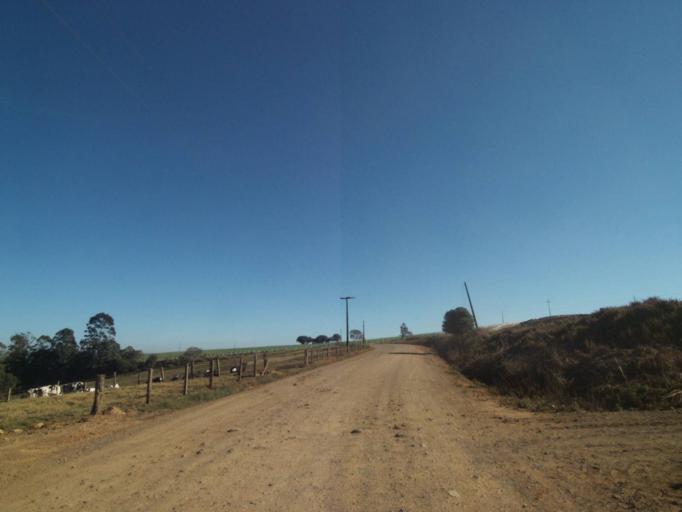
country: BR
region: Parana
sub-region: Tibagi
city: Tibagi
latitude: -24.5271
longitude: -50.3812
